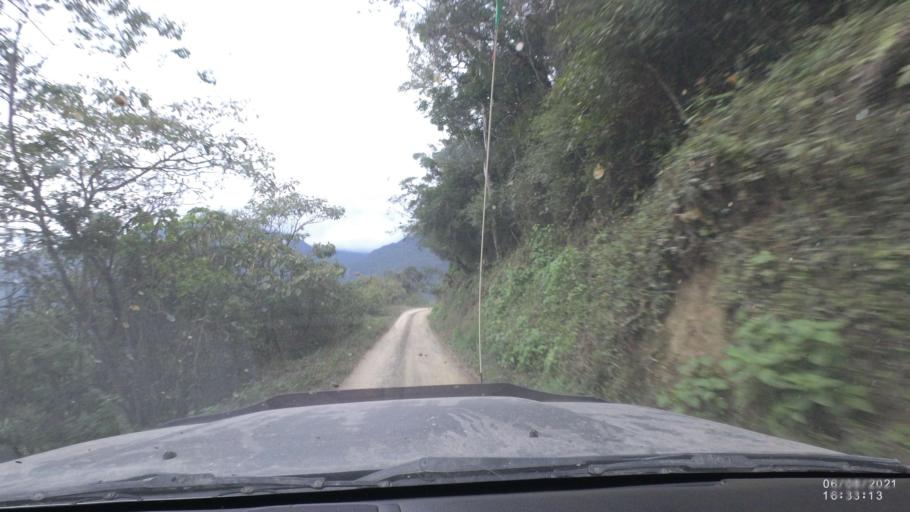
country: BO
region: La Paz
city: Quime
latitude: -16.5277
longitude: -66.7617
